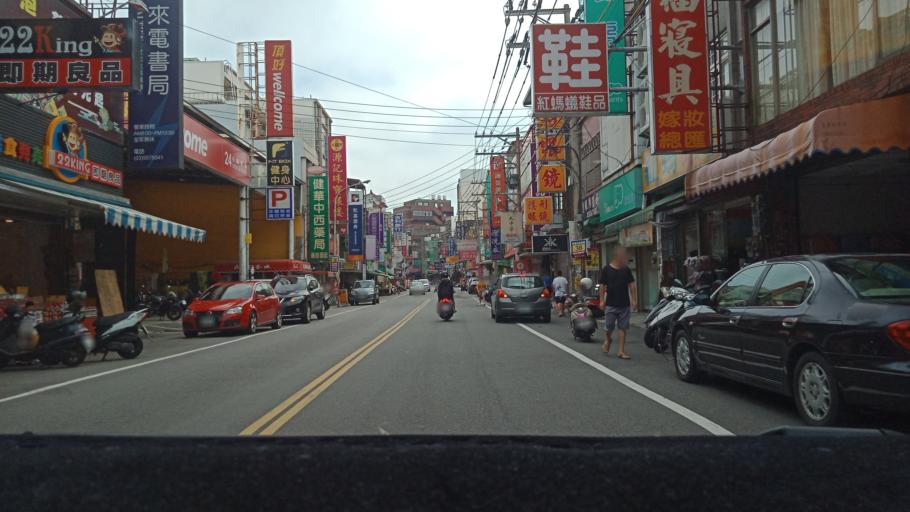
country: TW
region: Taiwan
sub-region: Hsinchu
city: Zhubei
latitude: 24.8729
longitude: 120.9950
